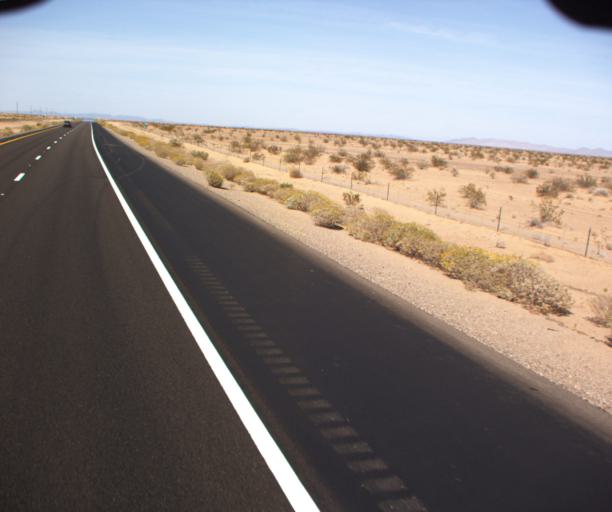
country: US
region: Arizona
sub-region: Yuma County
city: Somerton
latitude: 32.5206
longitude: -114.5617
